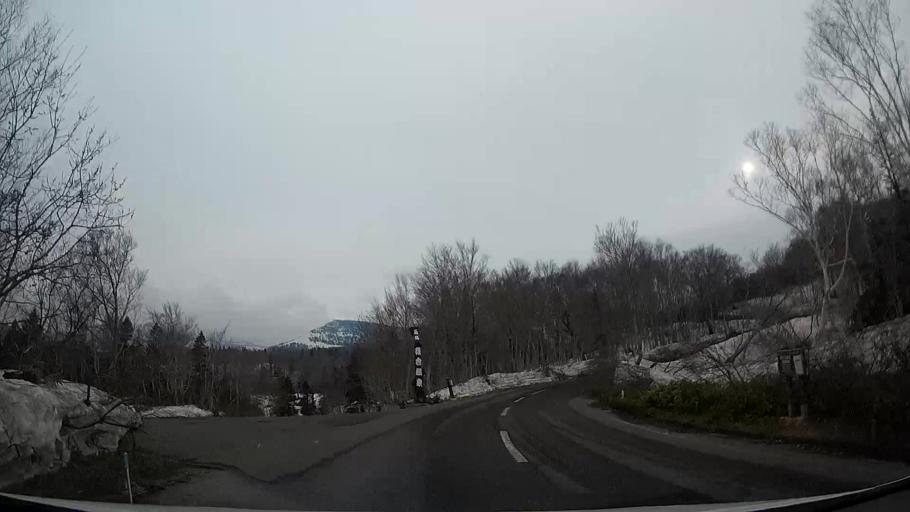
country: JP
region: Aomori
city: Aomori Shi
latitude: 40.6312
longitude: 140.9091
